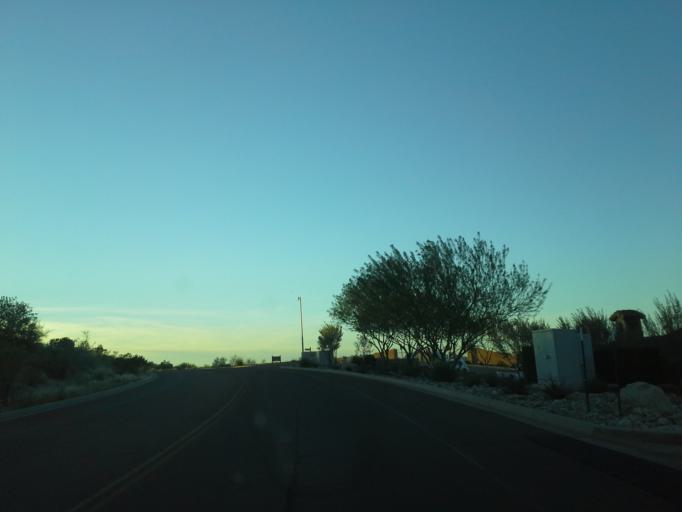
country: US
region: Arizona
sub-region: Pinal County
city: Apache Junction
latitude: 33.3818
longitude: -111.4457
